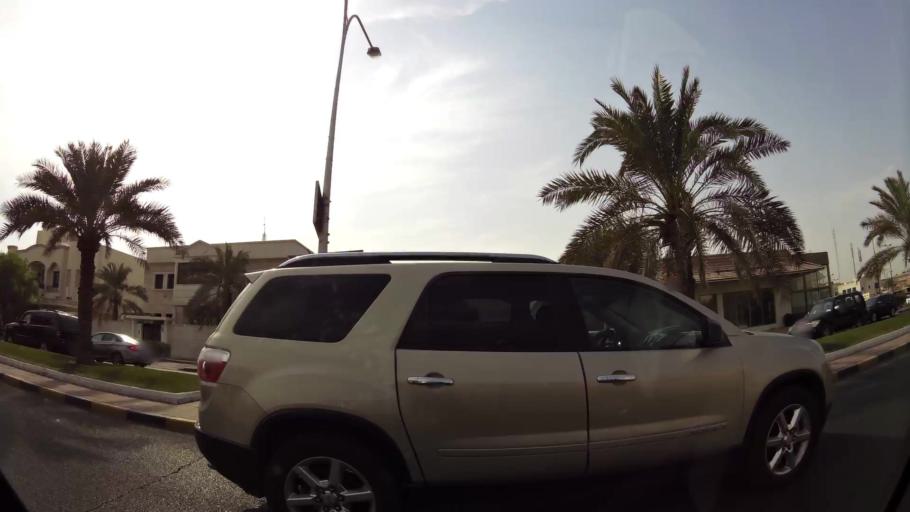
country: KW
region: Al Farwaniyah
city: Al Farwaniyah
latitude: 29.3091
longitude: 47.9708
